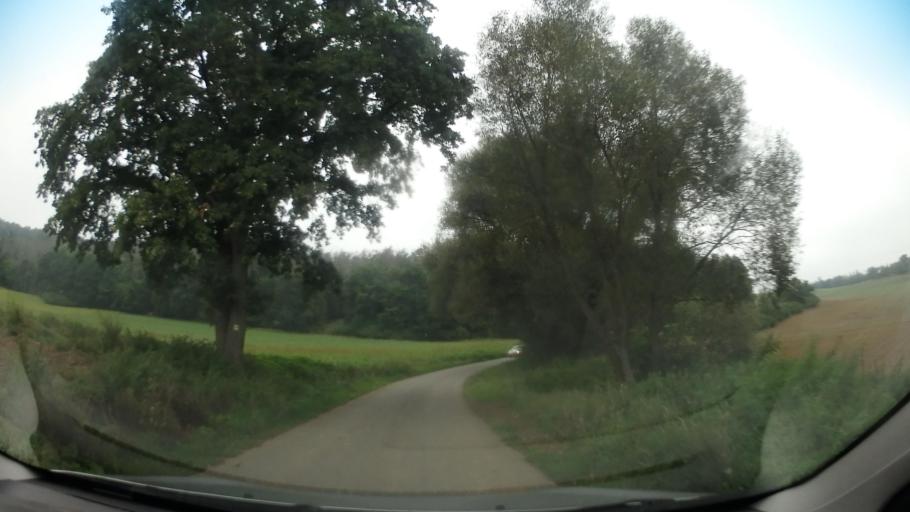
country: CZ
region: Central Bohemia
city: Sedlcany
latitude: 49.7165
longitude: 14.3699
